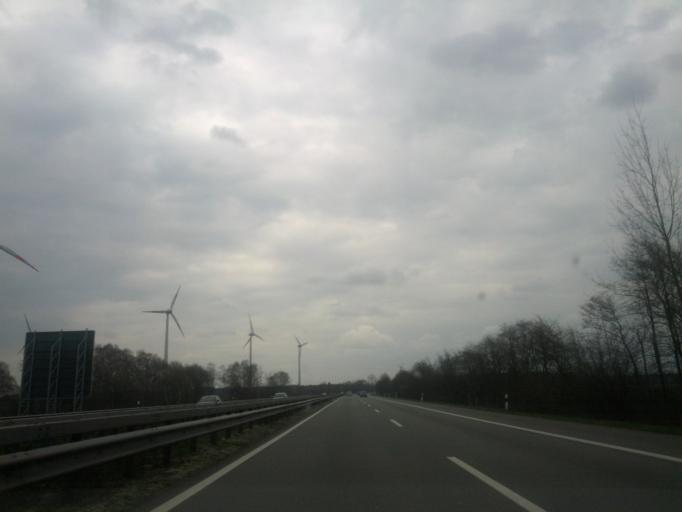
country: DE
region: Lower Saxony
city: Hatten
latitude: 53.0609
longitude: 8.3689
